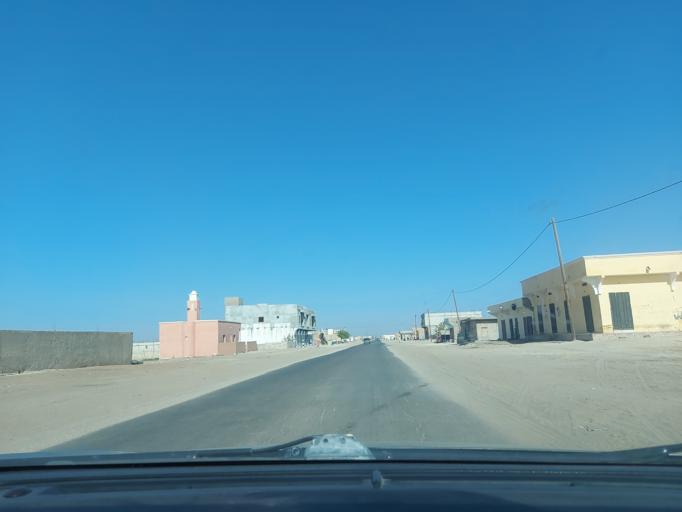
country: MR
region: Nouakchott
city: Nouakchott
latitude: 18.0104
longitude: -15.9788
